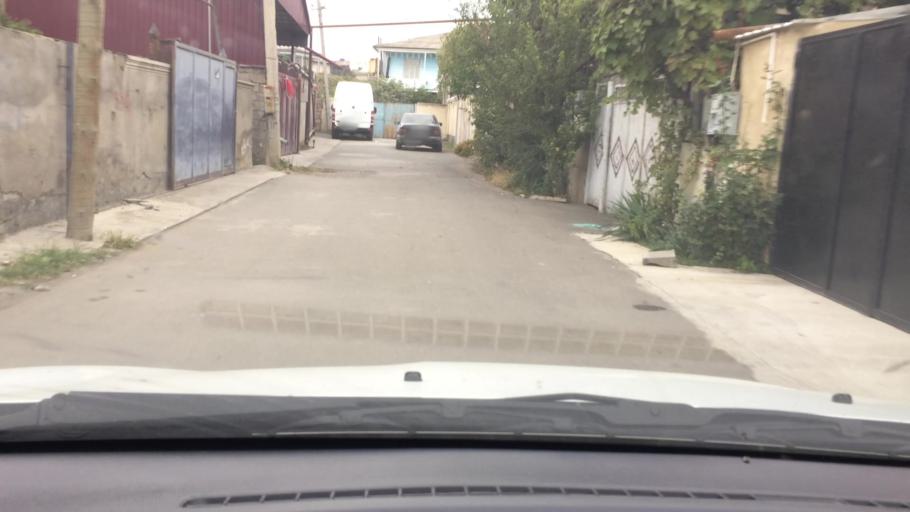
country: GE
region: Kvemo Kartli
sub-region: Marneuli
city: Marneuli
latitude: 41.4828
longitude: 44.7995
